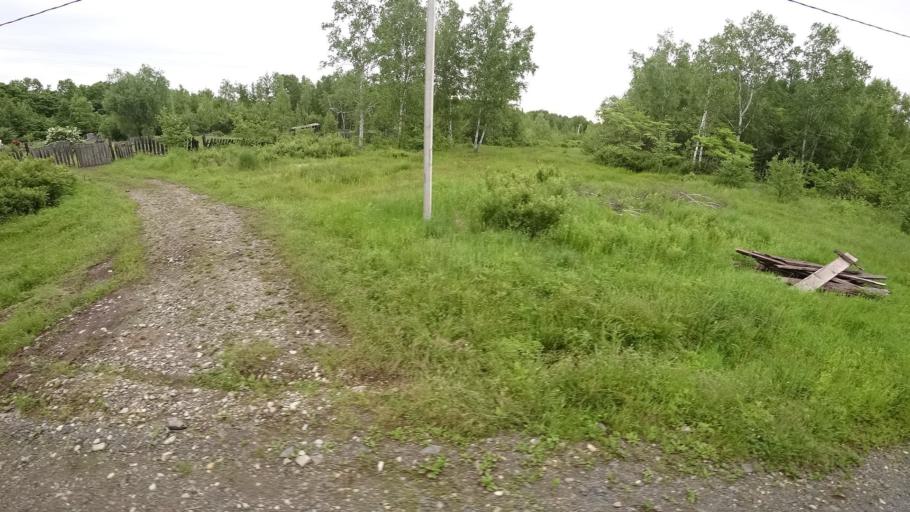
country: RU
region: Khabarovsk Krai
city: Amursk
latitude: 49.9042
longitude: 136.1355
